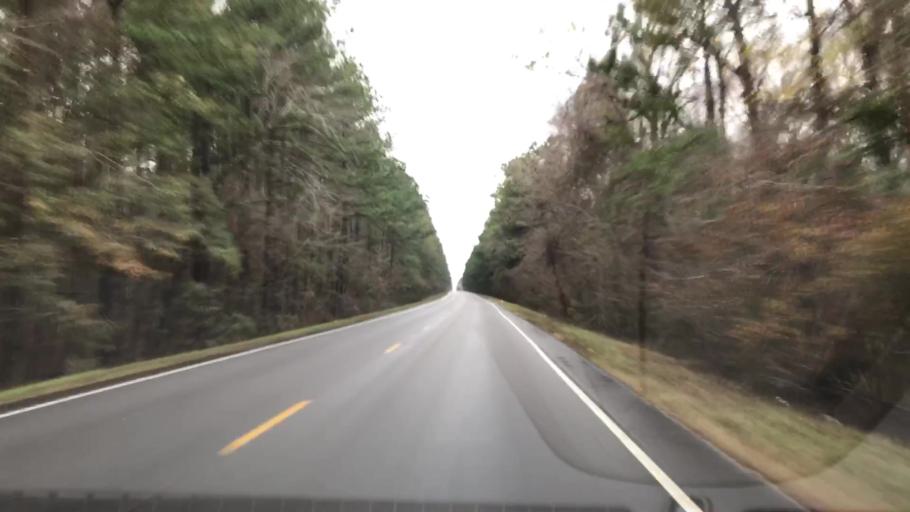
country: US
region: South Carolina
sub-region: Berkeley County
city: Saint Stephen
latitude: 33.2901
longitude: -79.7957
